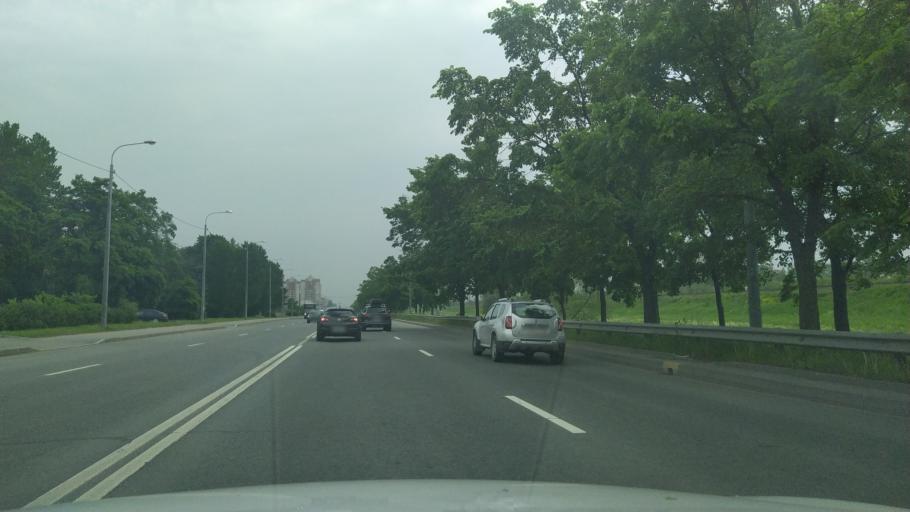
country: RU
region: St.-Petersburg
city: Kupchino
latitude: 59.8698
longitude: 30.3581
